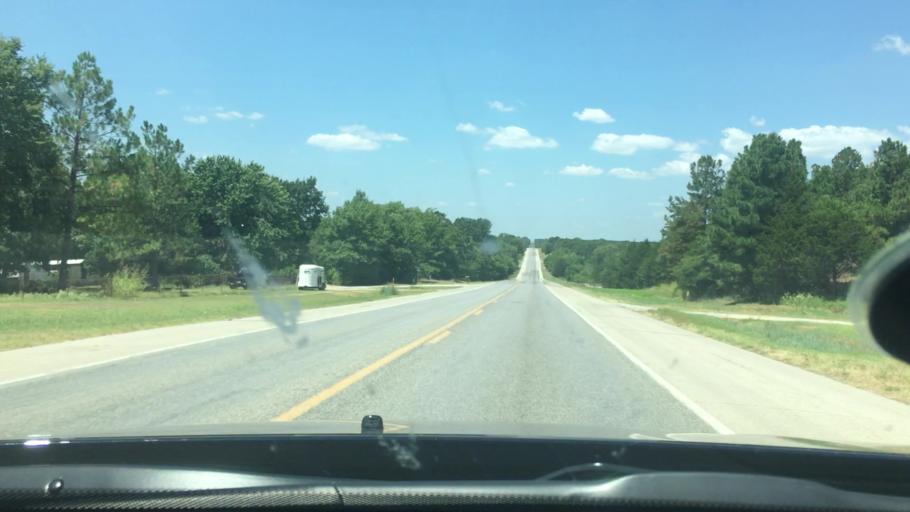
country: US
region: Oklahoma
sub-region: Carter County
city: Dickson
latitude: 34.1873
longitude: -96.9144
